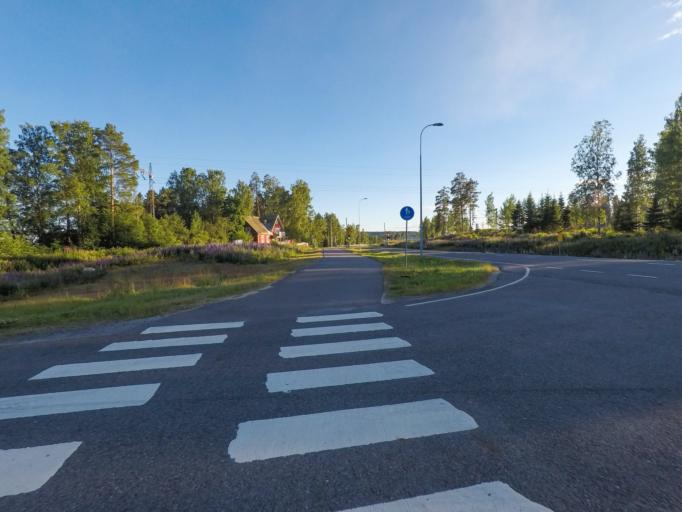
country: FI
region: Northern Savo
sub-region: Kuopio
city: Kuopio
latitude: 62.9562
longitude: 27.6907
